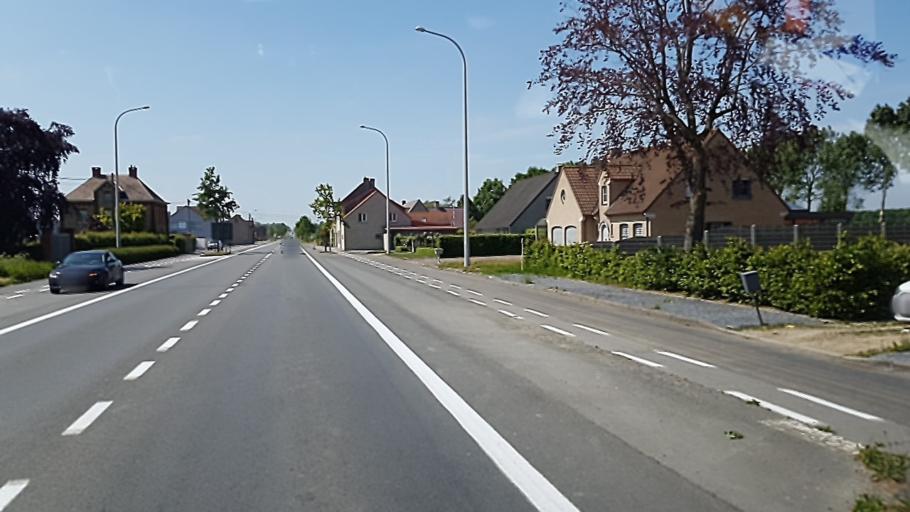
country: BE
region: Flanders
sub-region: Provincie West-Vlaanderen
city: Zonnebeke
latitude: 50.8283
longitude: 3.0128
